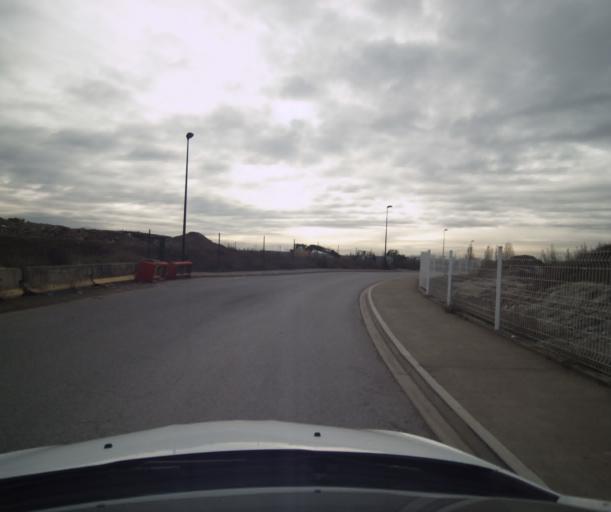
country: FR
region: Midi-Pyrenees
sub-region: Departement de la Haute-Garonne
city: Lespinasse
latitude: 43.7140
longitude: 1.3988
